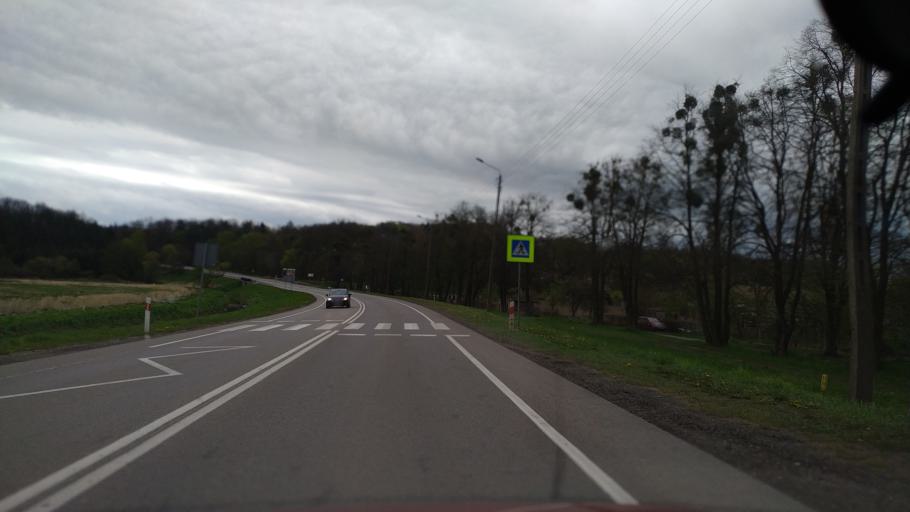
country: PL
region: Pomeranian Voivodeship
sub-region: Powiat starogardzki
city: Starogard Gdanski
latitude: 53.9717
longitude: 18.5505
